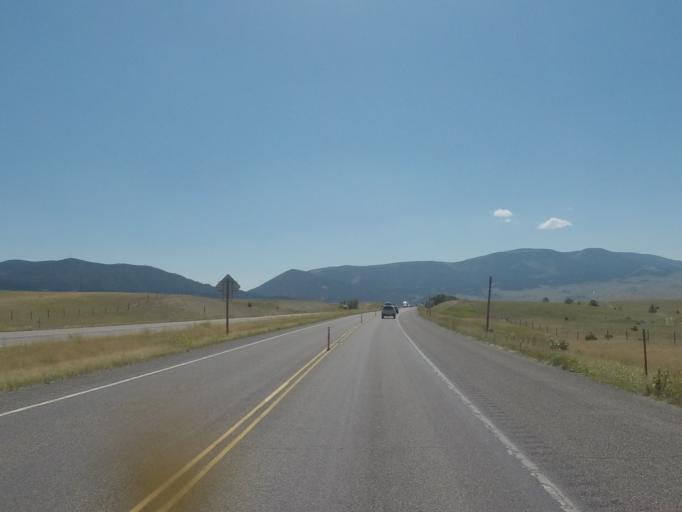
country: US
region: Montana
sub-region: Park County
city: Livingston
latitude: 45.6564
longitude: -110.5365
